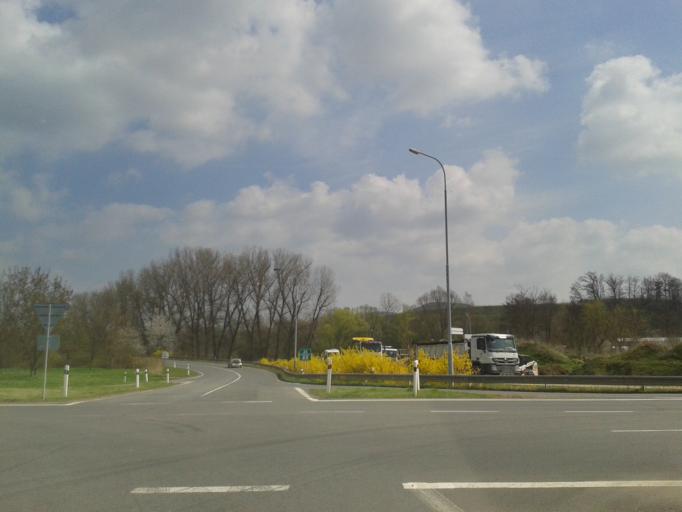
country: CZ
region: Central Bohemia
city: Zdice
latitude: 49.9007
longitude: 13.9614
